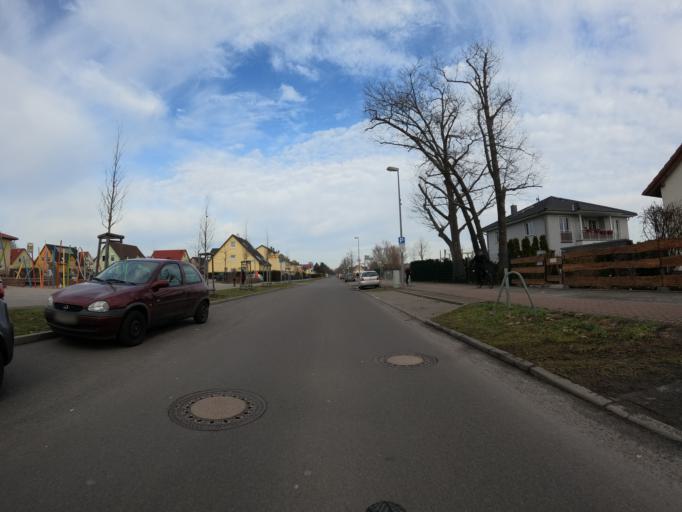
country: DE
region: Berlin
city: Mahlsdorf
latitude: 52.5179
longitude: 13.6326
